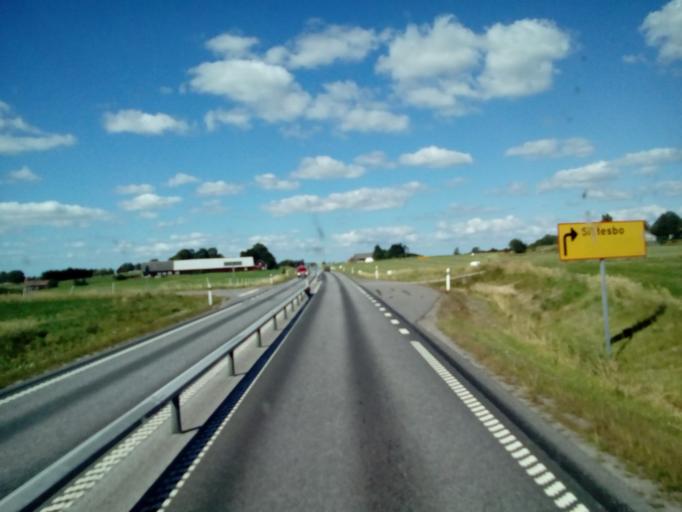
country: SE
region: OEstergoetland
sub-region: Linkopings Kommun
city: Malmslatt
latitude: 58.3306
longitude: 15.5620
